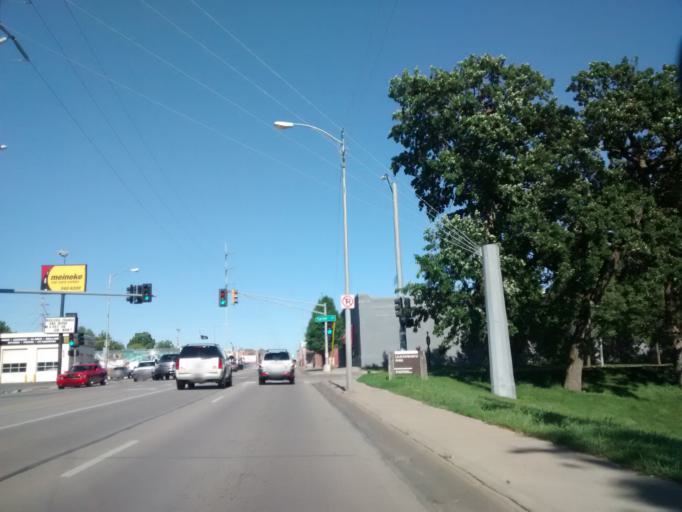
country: US
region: Nebraska
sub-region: Douglas County
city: Omaha
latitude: 41.2524
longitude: -95.9632
